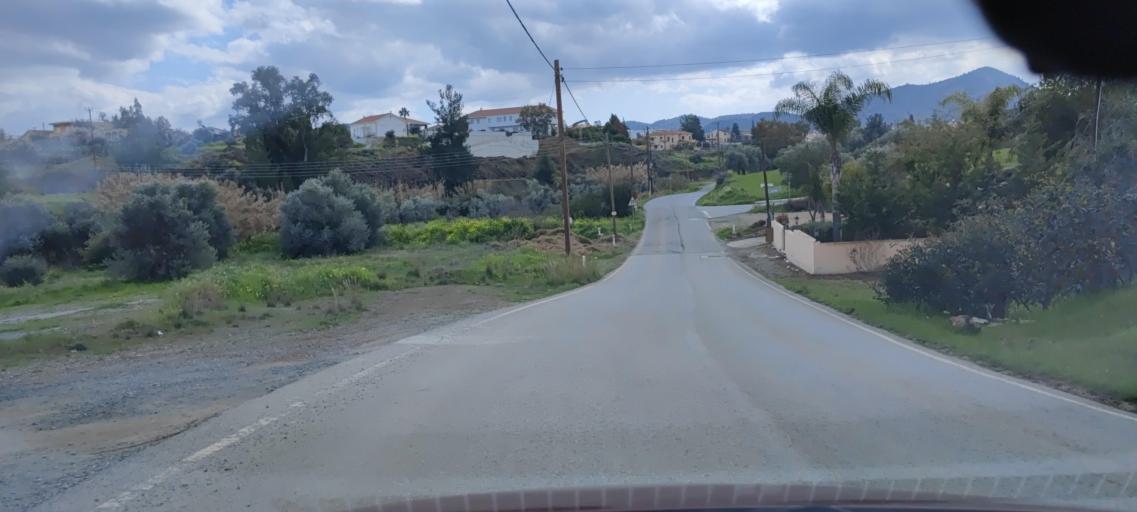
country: CY
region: Lefkosia
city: Lythrodontas
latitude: 34.9575
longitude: 33.2950
